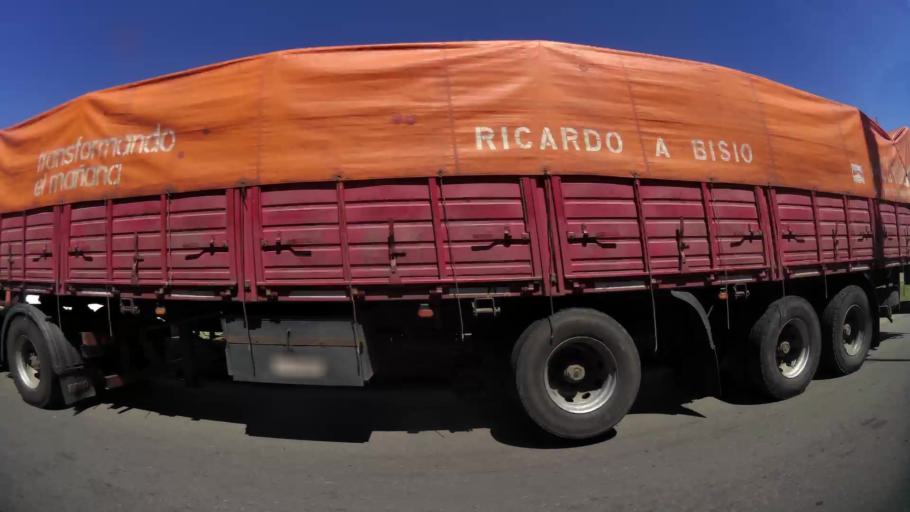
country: AR
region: Santa Fe
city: Perez
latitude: -32.9618
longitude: -60.7118
